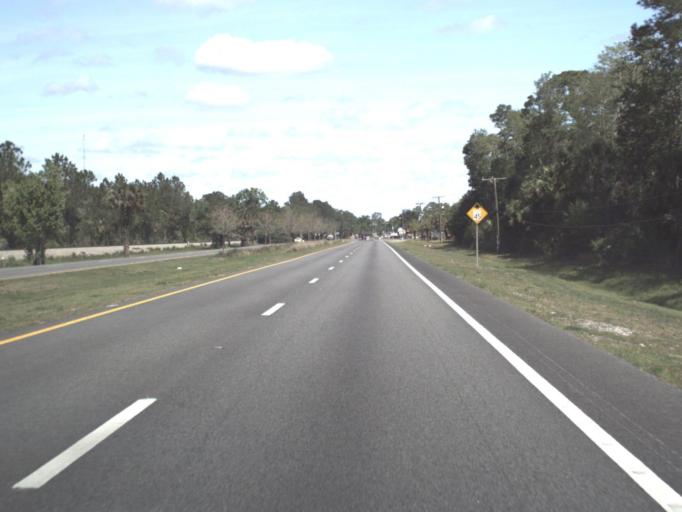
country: US
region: Florida
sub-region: Flagler County
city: Bunnell
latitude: 29.4539
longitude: -81.2474
